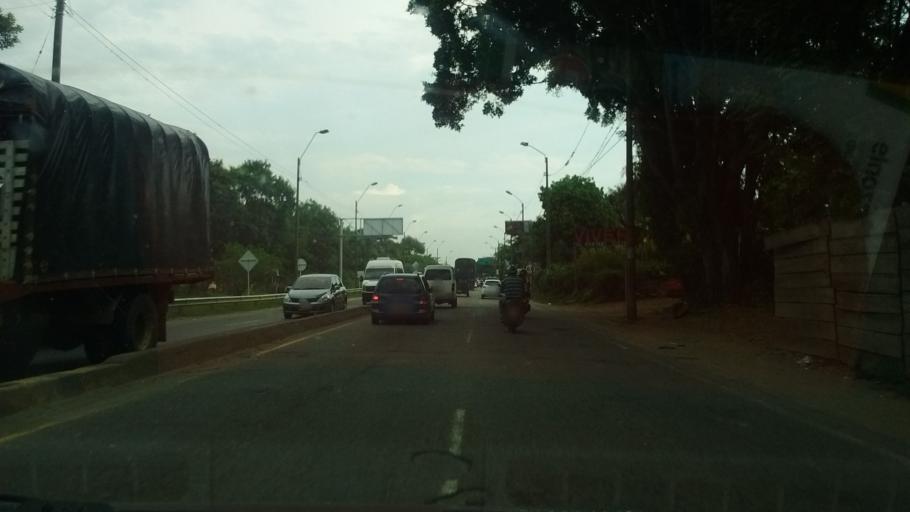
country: CO
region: Valle del Cauca
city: Jamundi
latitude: 3.3435
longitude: -76.5243
